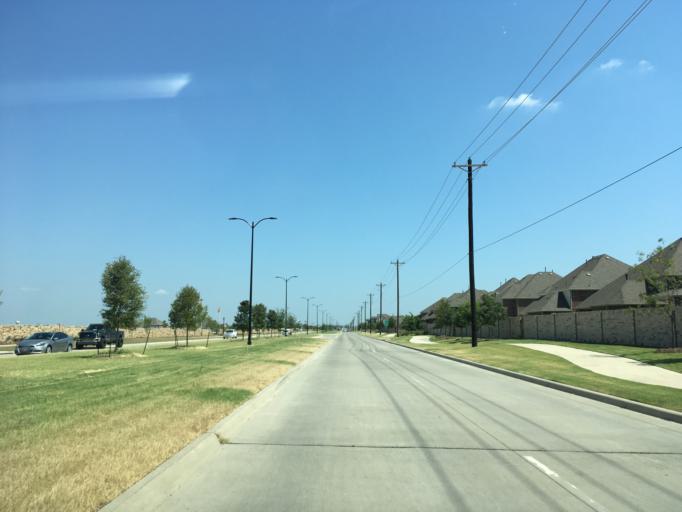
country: US
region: Texas
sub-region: Collin County
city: Prosper
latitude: 33.1934
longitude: -96.7677
